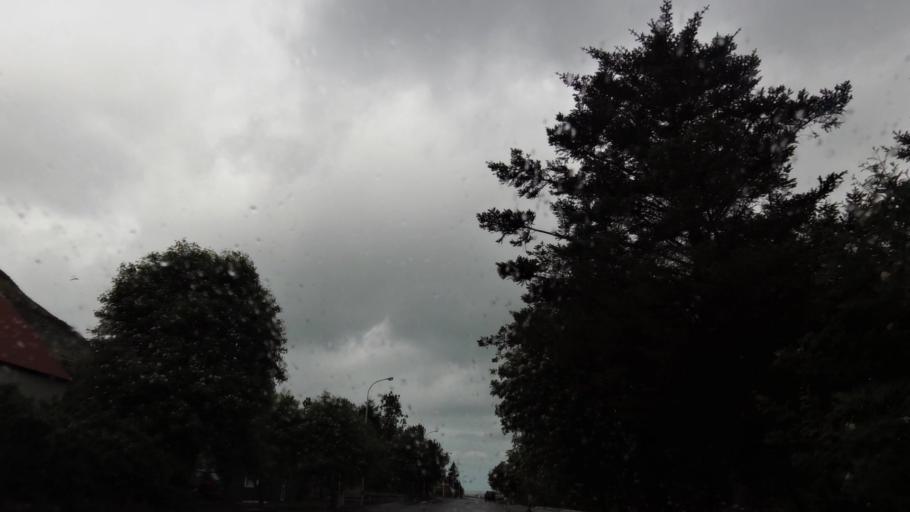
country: IS
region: Westfjords
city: Isafjoerdur
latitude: 65.8784
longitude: -23.4963
